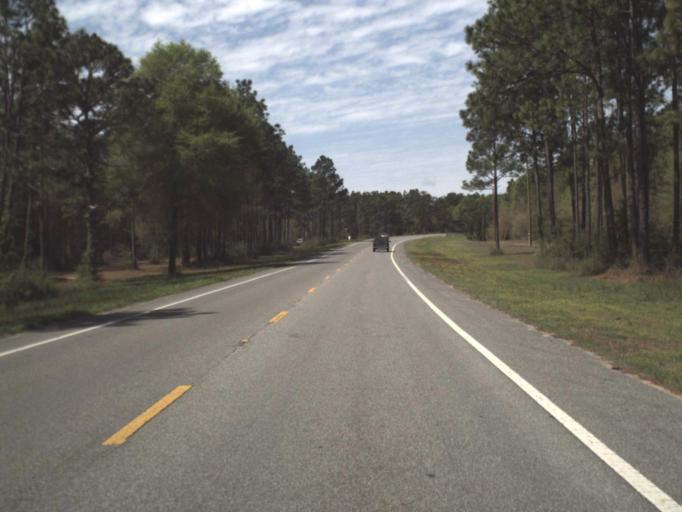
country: US
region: Florida
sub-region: Okaloosa County
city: Crestview
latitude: 30.7223
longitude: -86.6729
